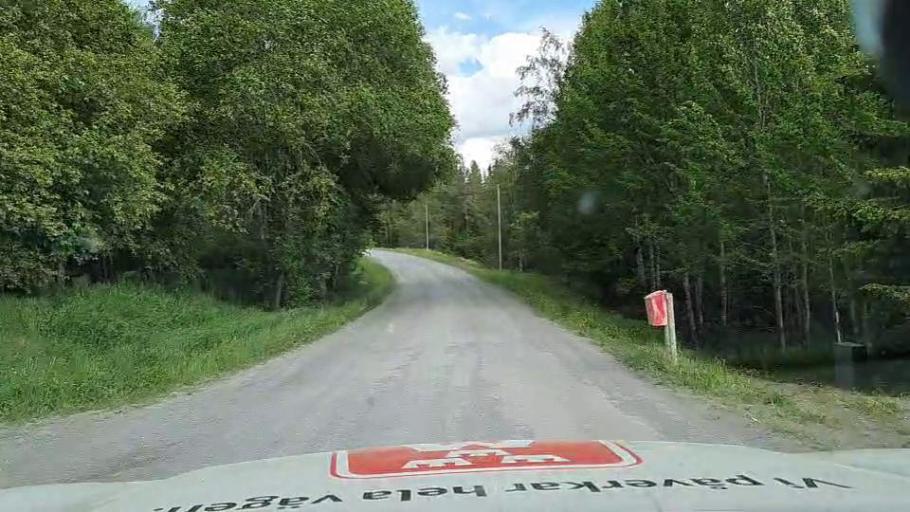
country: SE
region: Jaemtland
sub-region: OEstersunds Kommun
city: Lit
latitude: 63.2844
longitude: 14.7361
